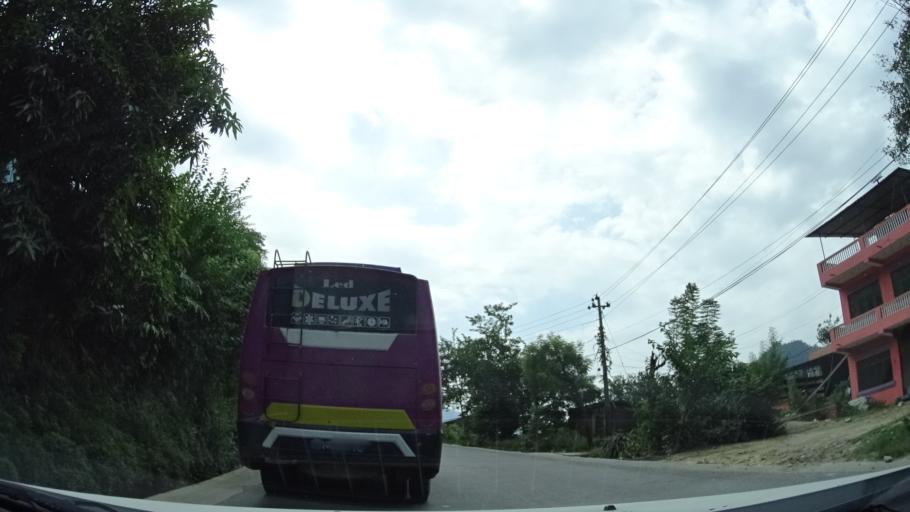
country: NP
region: Central Region
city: Kirtipur
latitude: 27.8109
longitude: 84.9448
